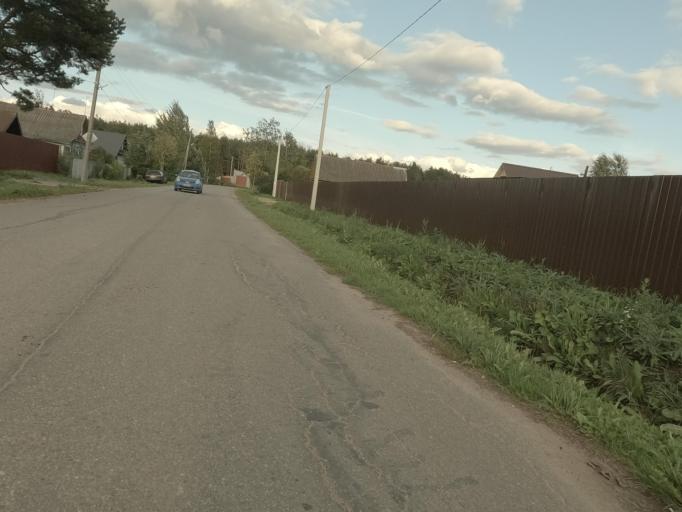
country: RU
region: Leningrad
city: Mga
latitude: 59.7606
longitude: 31.0742
